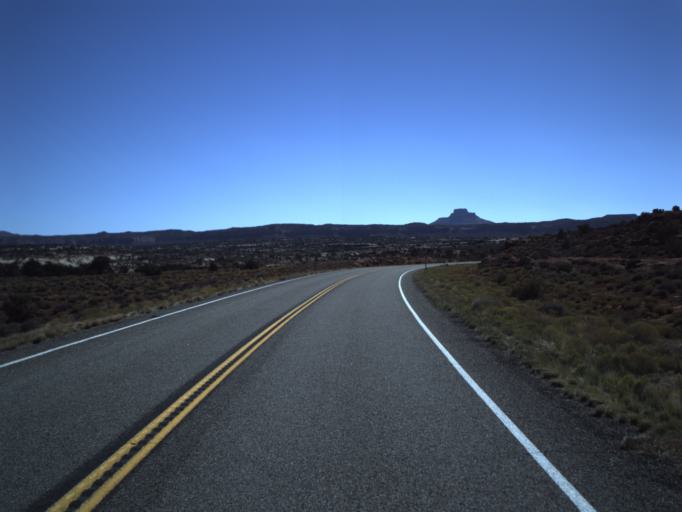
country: US
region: Utah
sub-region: San Juan County
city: Blanding
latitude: 37.8019
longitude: -110.3092
